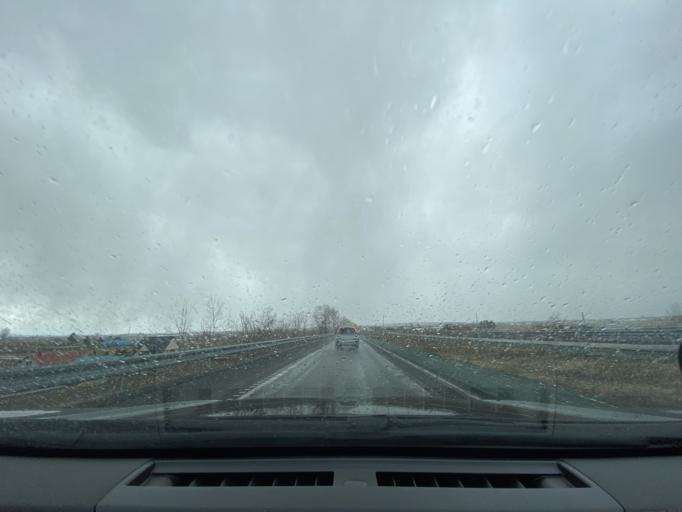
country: JP
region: Hokkaido
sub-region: Asahikawa-shi
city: Asahikawa
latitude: 43.8604
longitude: 142.4401
